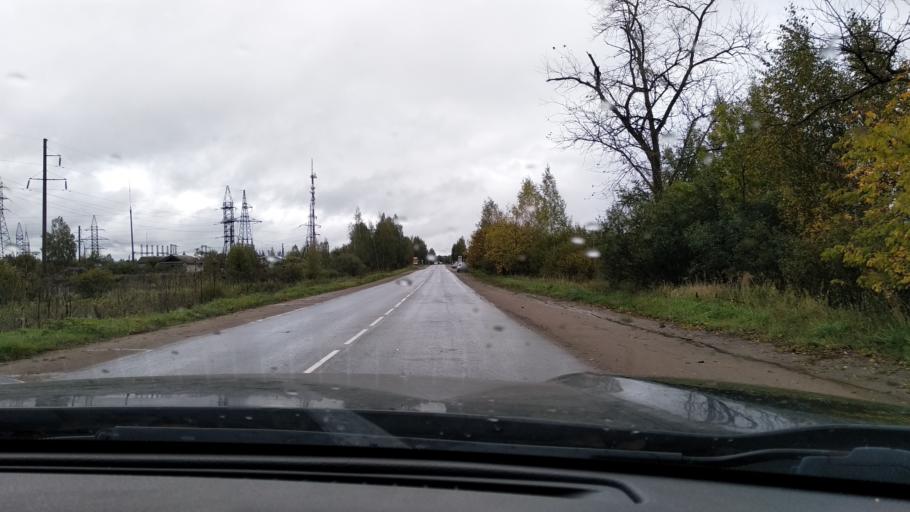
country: RU
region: Tverskaya
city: Kashin
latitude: 57.3585
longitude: 37.5755
